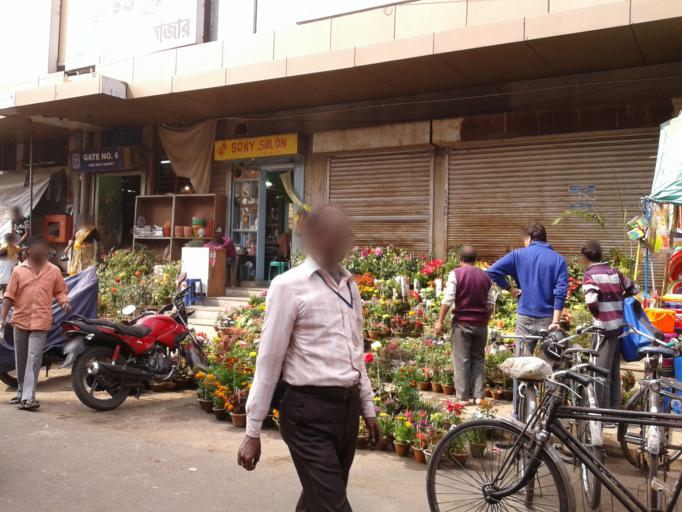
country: IN
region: West Bengal
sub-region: Kolkata
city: Kolkata
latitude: 22.5168
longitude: 88.3492
